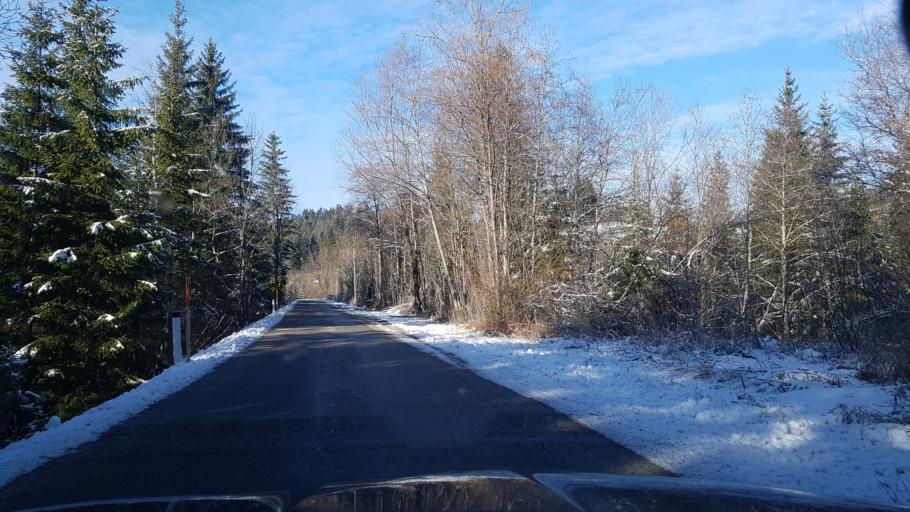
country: AT
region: Salzburg
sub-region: Politischer Bezirk Salzburg-Umgebung
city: Faistenau
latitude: 47.7728
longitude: 13.2232
